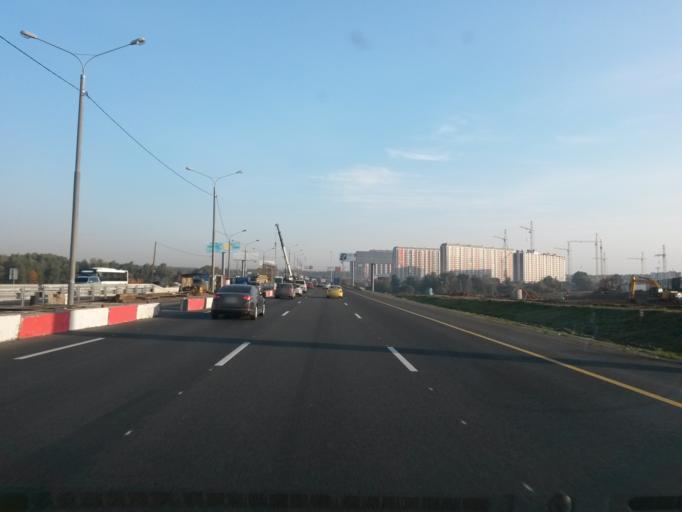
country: RU
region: Moskovskaya
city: Shcherbinka
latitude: 55.5239
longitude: 37.6098
